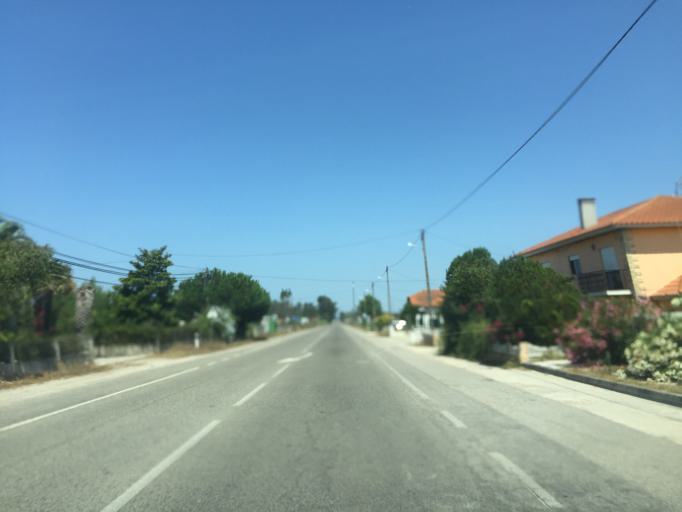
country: PT
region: Coimbra
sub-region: Mira
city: Mira
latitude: 40.3242
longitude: -8.7519
